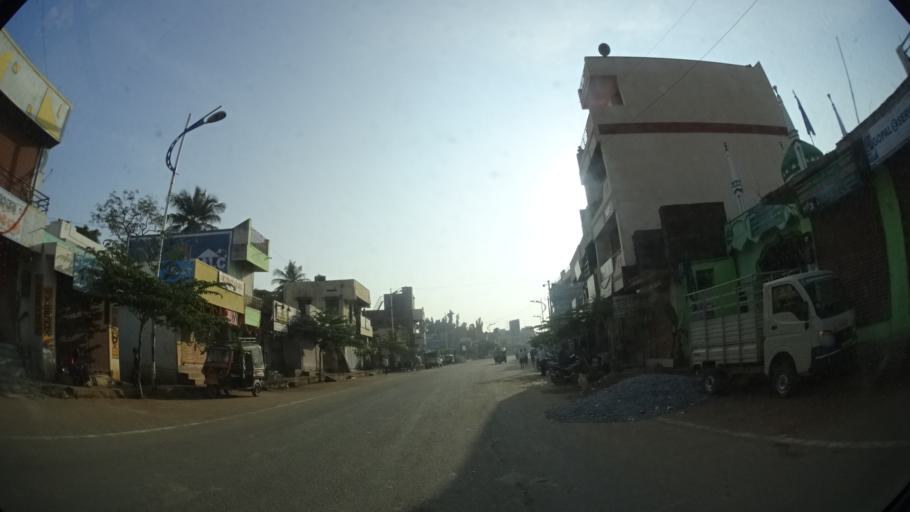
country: IN
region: Karnataka
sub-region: Bellary
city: Hospet
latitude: 15.2666
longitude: 76.3974
